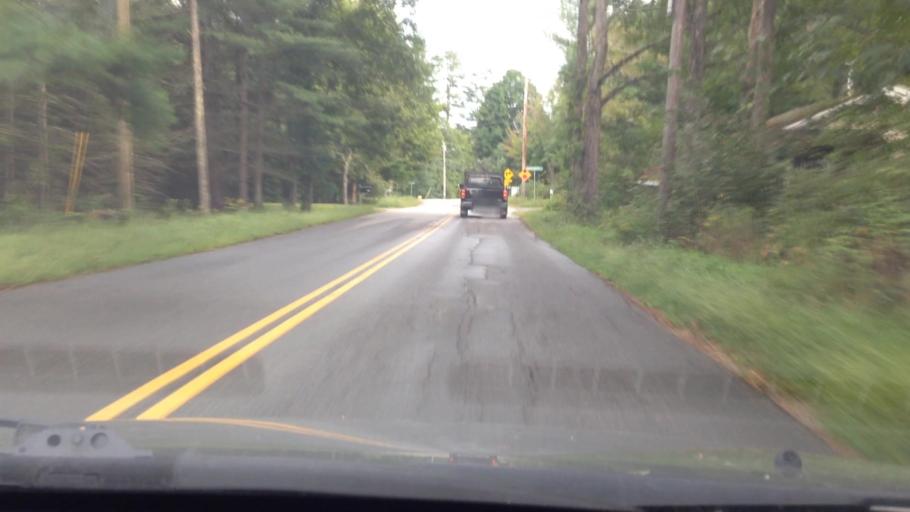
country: US
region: New Hampshire
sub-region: Cheshire County
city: Swanzey
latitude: 42.8876
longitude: -72.2892
